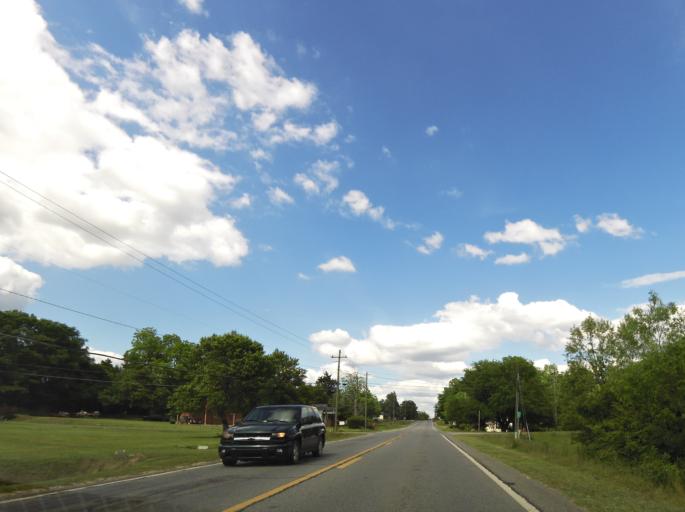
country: US
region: Georgia
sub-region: Treutlen County
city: Soperton
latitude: 32.3736
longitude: -82.6021
